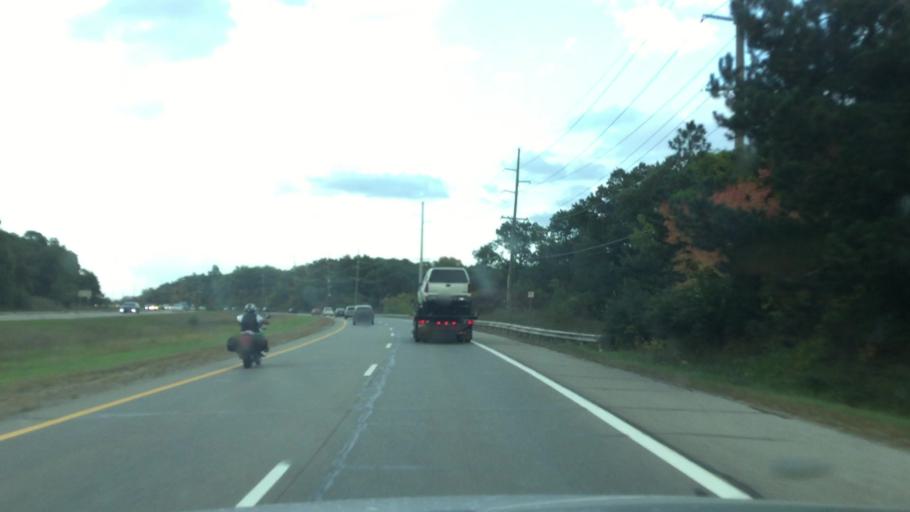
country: US
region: Michigan
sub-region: Oakland County
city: Milford
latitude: 42.6430
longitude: -83.6017
